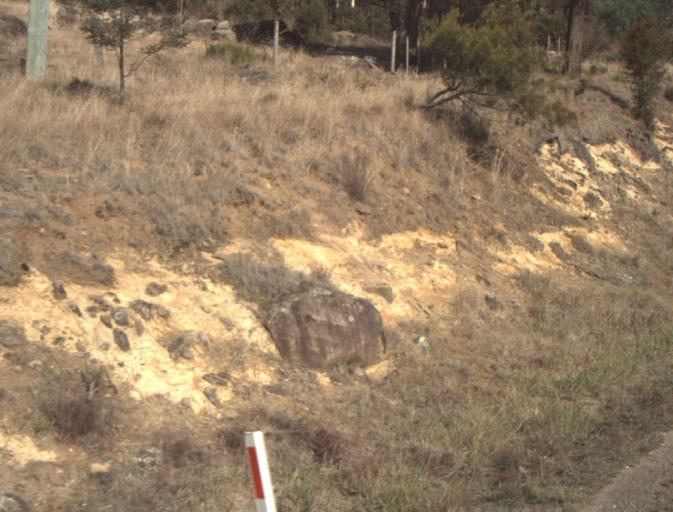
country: AU
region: Tasmania
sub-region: Launceston
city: Mayfield
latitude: -41.2637
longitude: 147.2168
